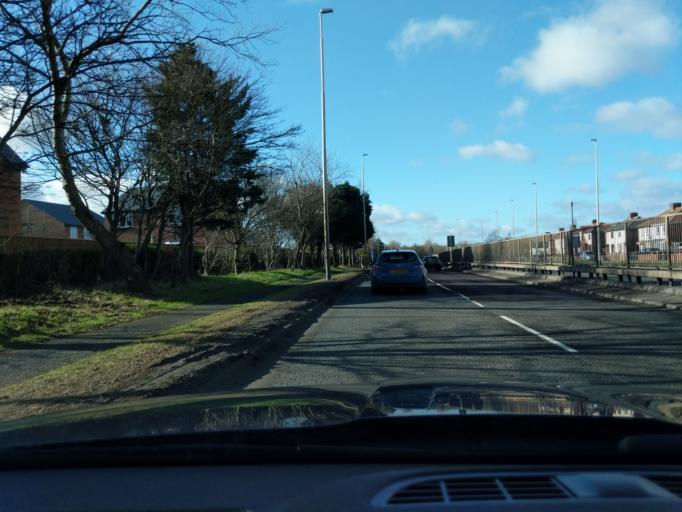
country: GB
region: England
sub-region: South Tyneside
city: Jarrow
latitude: 54.9646
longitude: -1.4761
